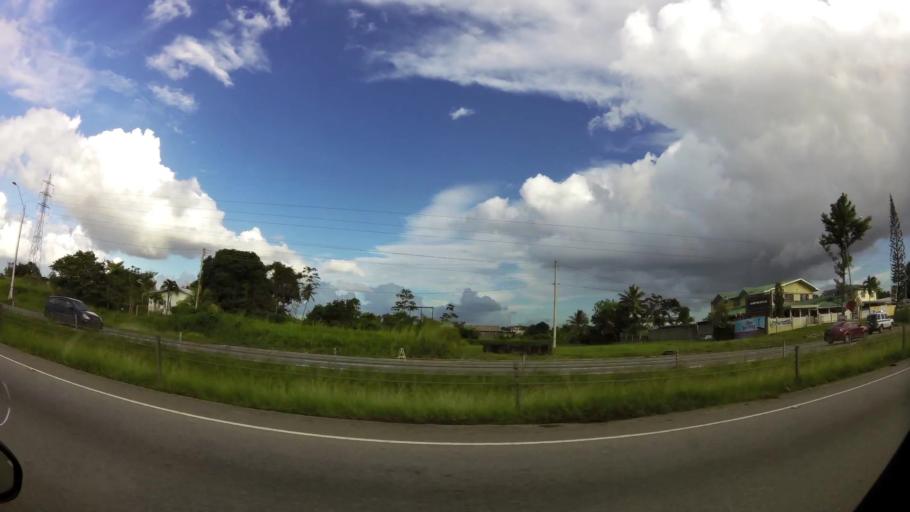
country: TT
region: Chaguanas
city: Chaguanas
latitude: 10.4551
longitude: -61.4106
